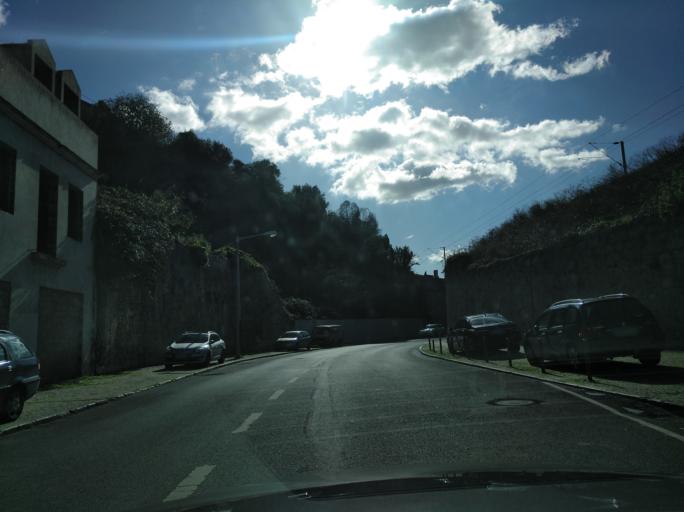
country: PT
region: Lisbon
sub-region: Lisbon
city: Lisbon
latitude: 38.7333
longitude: -9.1172
